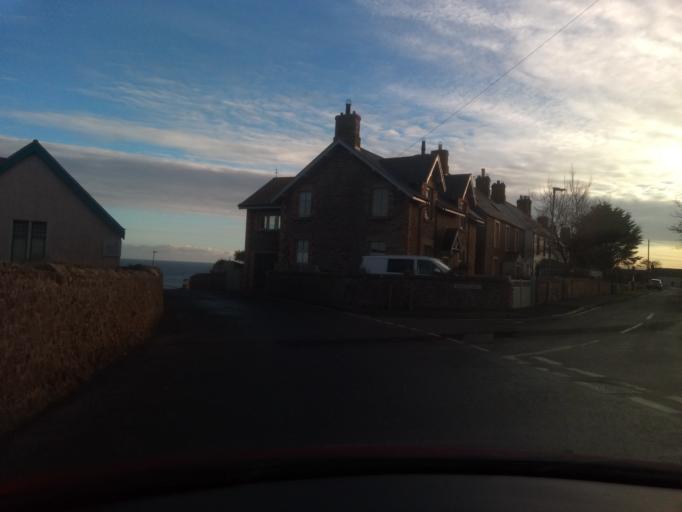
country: GB
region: Scotland
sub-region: The Scottish Borders
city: Eyemouth
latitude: 55.8996
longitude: -2.1324
